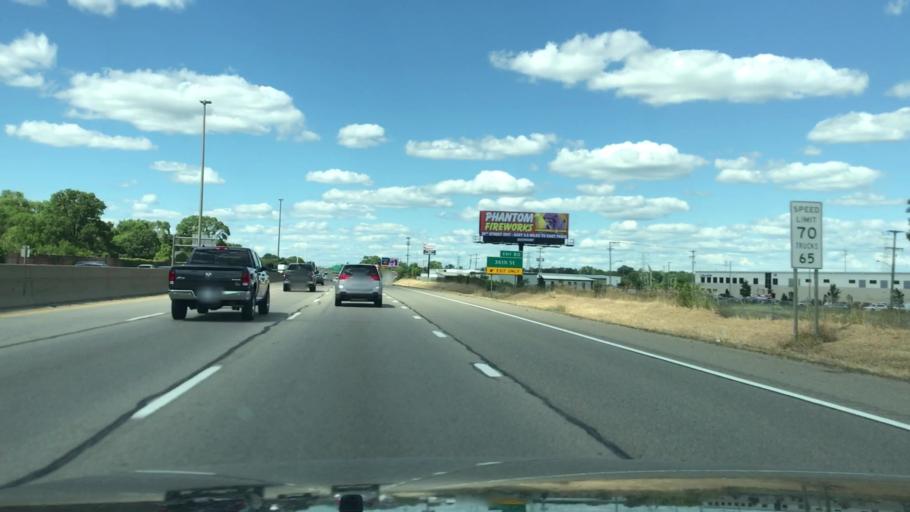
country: US
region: Michigan
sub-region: Kent County
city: Wyoming
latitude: 42.8915
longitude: -85.6786
